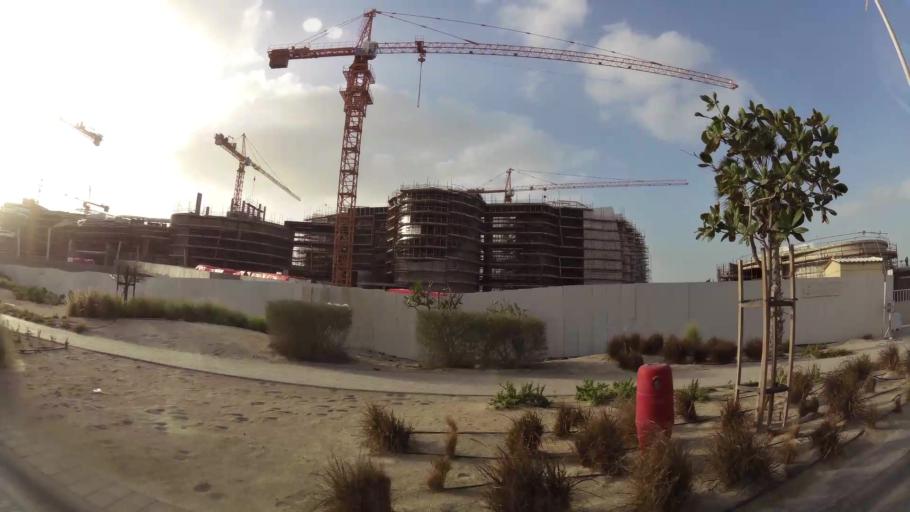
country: AE
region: Abu Dhabi
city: Abu Dhabi
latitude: 24.5602
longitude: 54.4534
